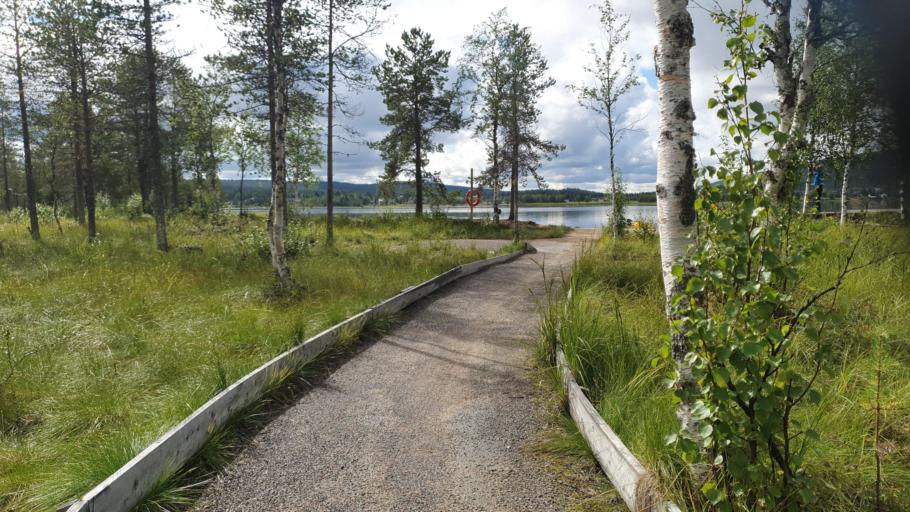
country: FI
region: Lapland
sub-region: Tunturi-Lappi
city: Kolari
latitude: 67.6124
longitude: 24.1683
